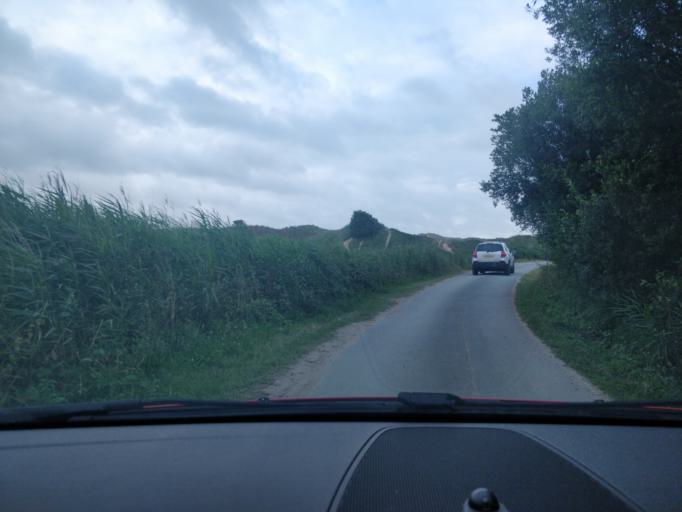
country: GB
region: Wales
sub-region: Gwynedd
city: Llanfair
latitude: 52.8130
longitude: -4.1417
